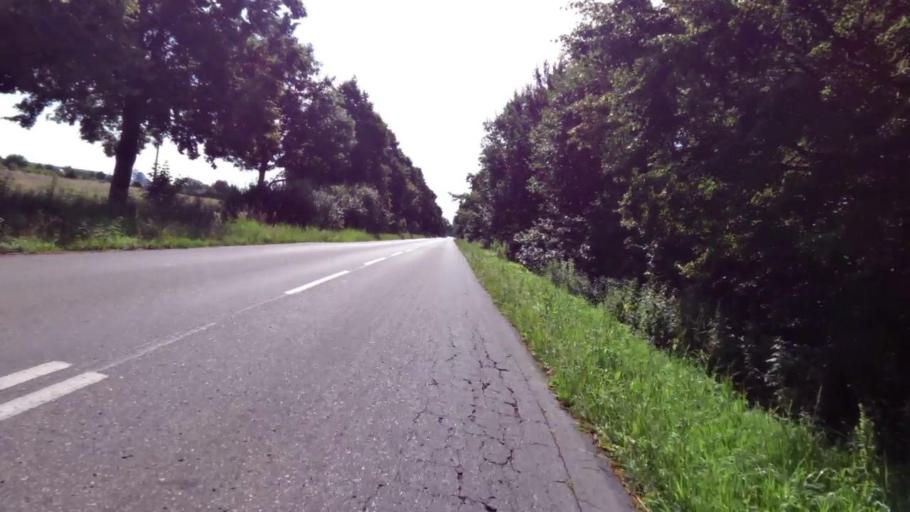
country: PL
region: West Pomeranian Voivodeship
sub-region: Powiat stargardzki
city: Dobrzany
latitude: 53.3631
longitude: 15.4161
